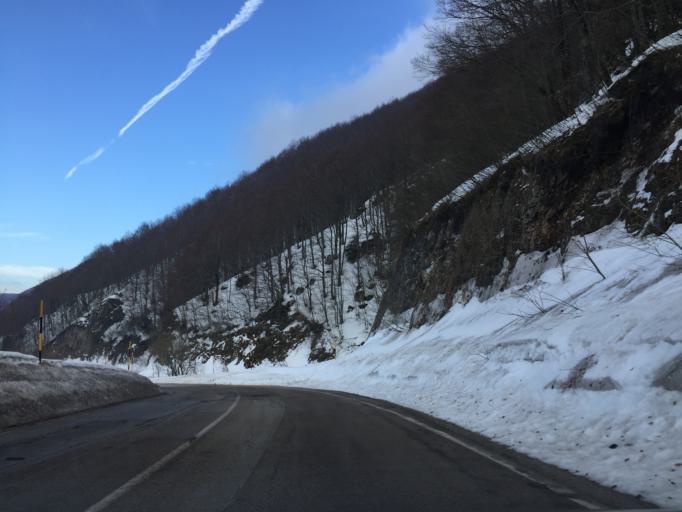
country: IT
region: Molise
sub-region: Provincia di Campobasso
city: San Massimo
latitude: 41.4675
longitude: 14.4018
